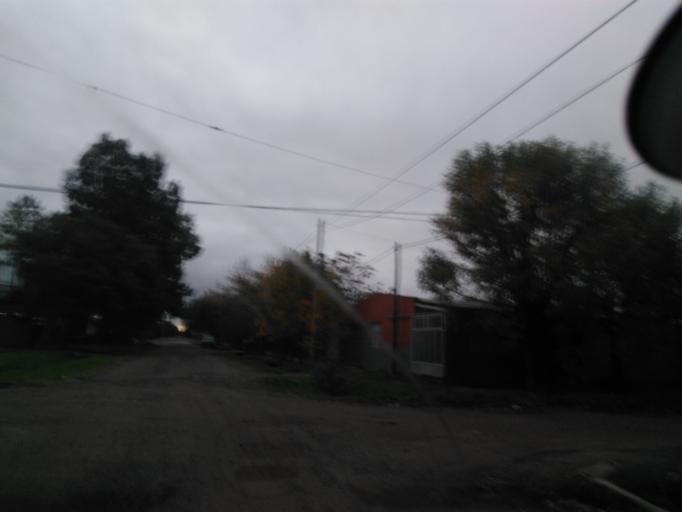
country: AR
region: Chaco
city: Resistencia
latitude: -27.4792
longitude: -58.9963
